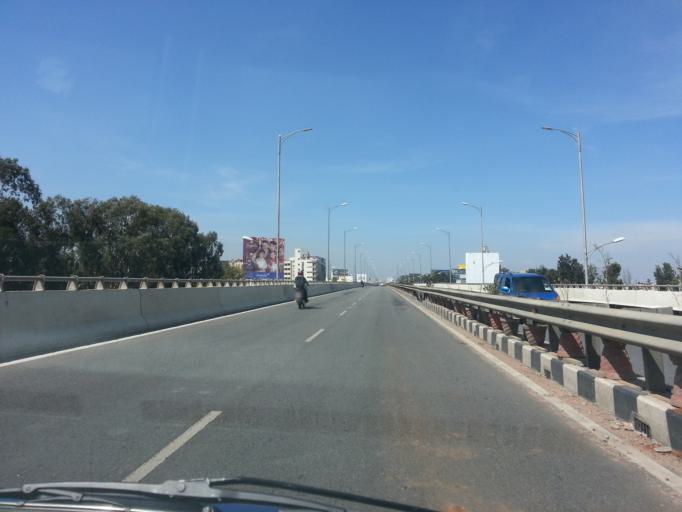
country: IN
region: Karnataka
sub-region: Bangalore Urban
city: Bangalore
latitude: 12.8660
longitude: 77.6565
